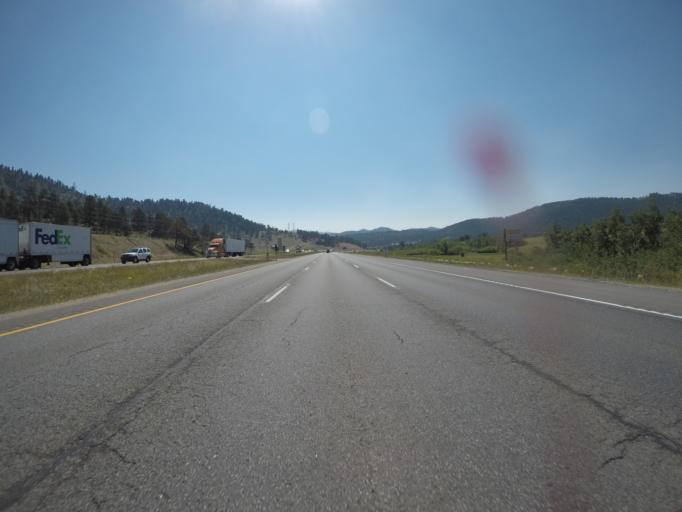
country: US
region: Colorado
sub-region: Clear Creek County
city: Idaho Springs
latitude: 39.7205
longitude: -105.4069
